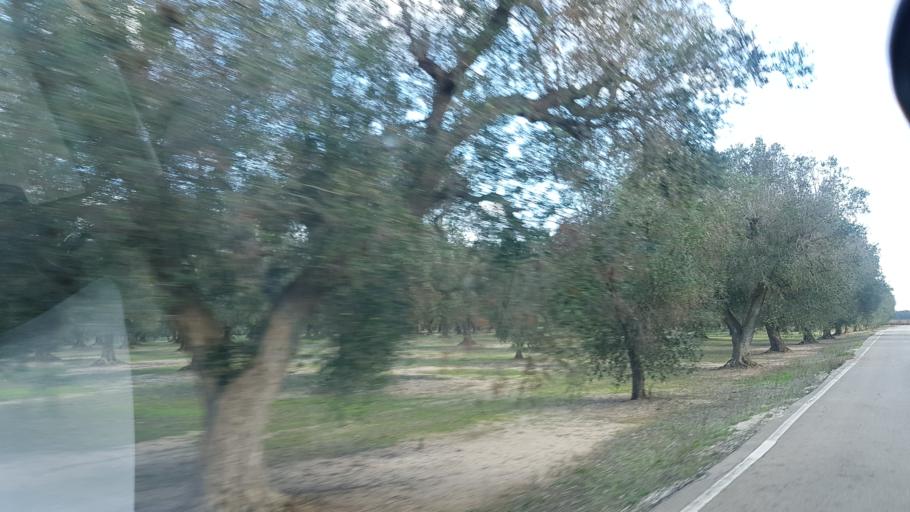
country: IT
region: Apulia
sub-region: Provincia di Brindisi
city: San Pietro Vernotico
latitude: 40.5132
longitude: 18.0159
